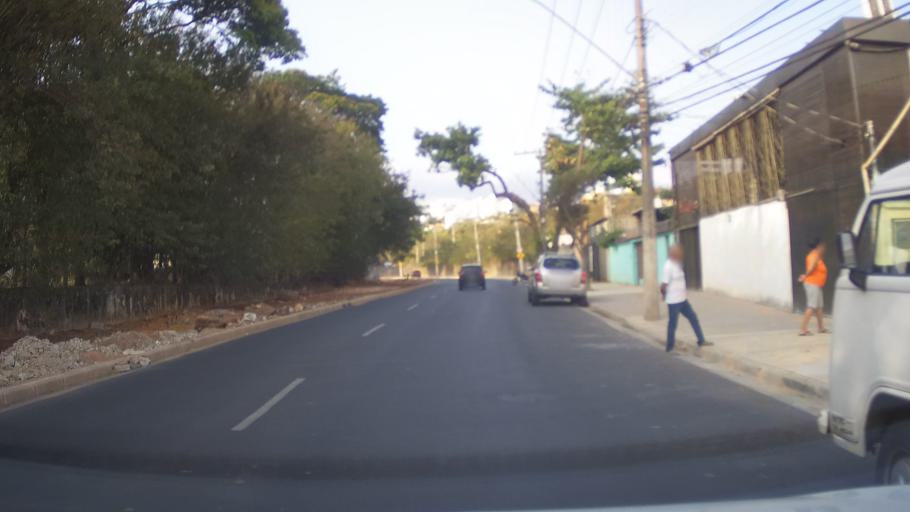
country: BR
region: Minas Gerais
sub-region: Belo Horizonte
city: Belo Horizonte
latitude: -19.8897
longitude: -43.9126
